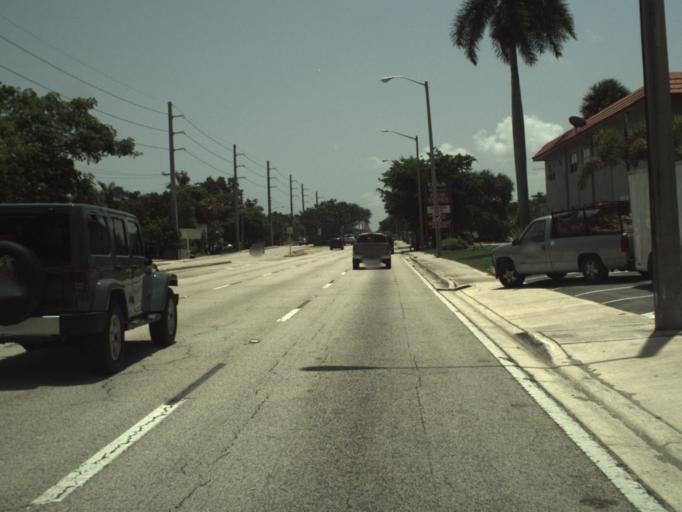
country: US
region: Florida
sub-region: Broward County
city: Wilton Manors
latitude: 26.1582
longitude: -80.1546
